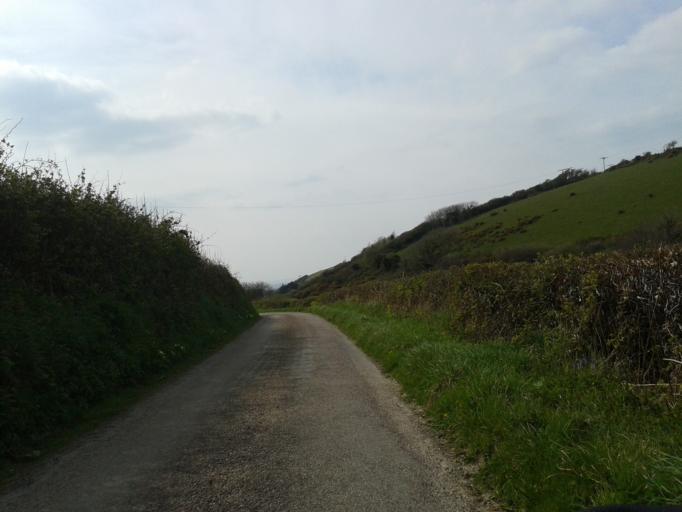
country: GB
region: England
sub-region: Devon
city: Braunton
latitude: 51.1302
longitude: -4.1983
